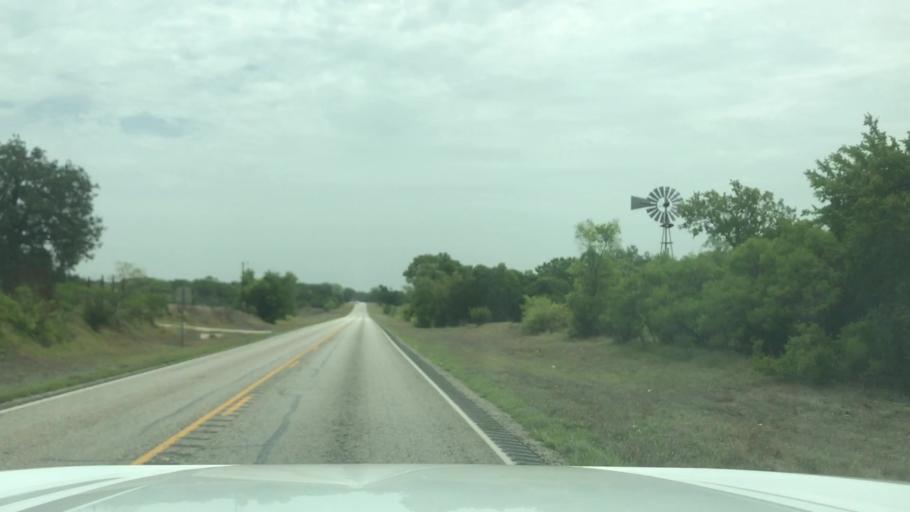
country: US
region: Texas
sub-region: Hamilton County
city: Hico
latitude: 32.0421
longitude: -98.1329
